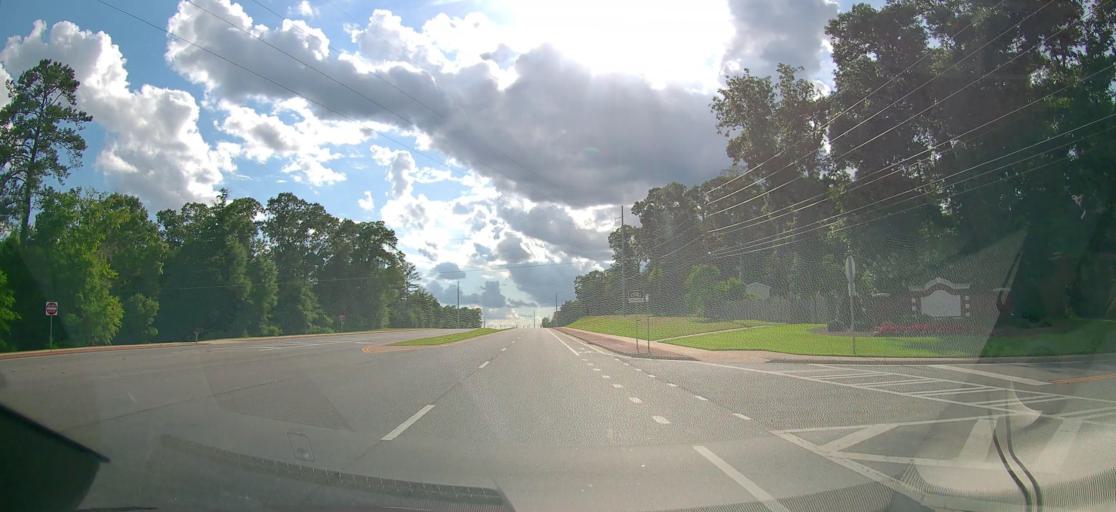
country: US
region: Georgia
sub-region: Houston County
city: Centerville
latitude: 32.5468
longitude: -83.7140
